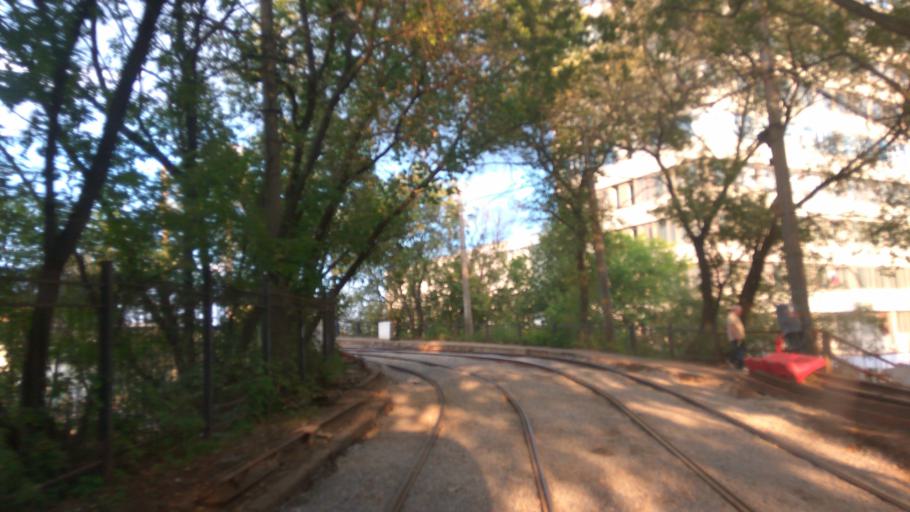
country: RU
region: Moskovskaya
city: Koptevo
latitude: 55.8145
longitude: 37.5030
